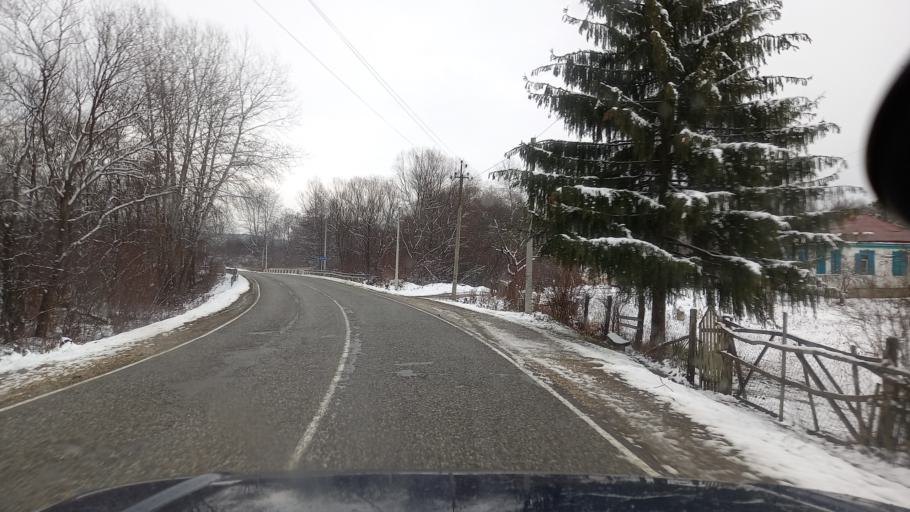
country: RU
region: Adygeya
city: Abadzekhskaya
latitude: 44.3597
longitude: 40.2943
